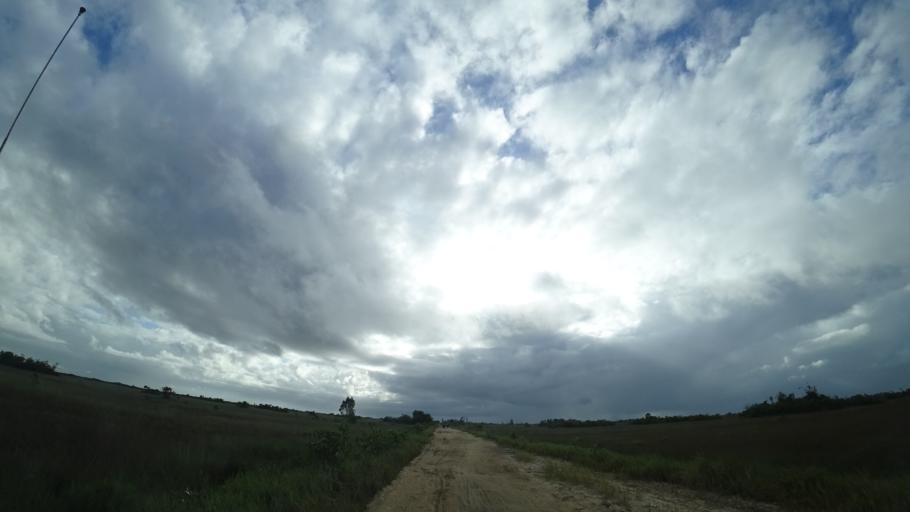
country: MZ
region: Sofala
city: Beira
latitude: -19.6966
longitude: 35.0326
